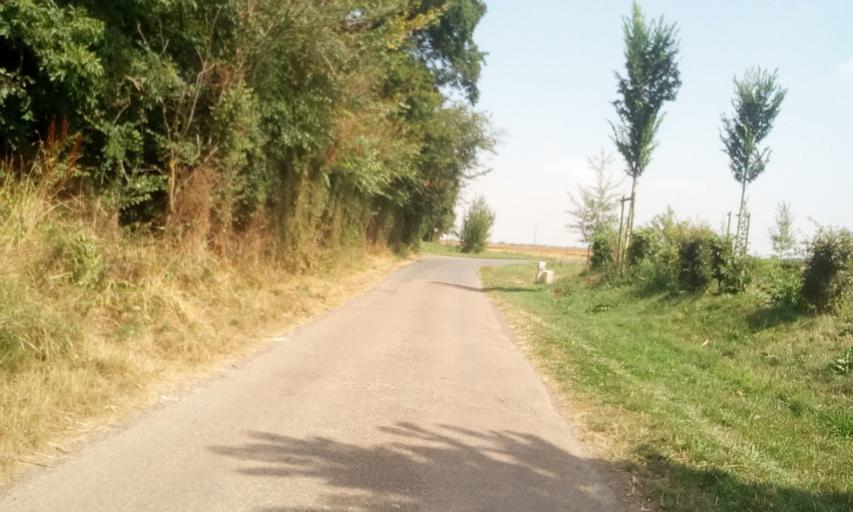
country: FR
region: Lower Normandy
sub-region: Departement du Calvados
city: Douvres-la-Delivrande
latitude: 49.2909
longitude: -0.4138
